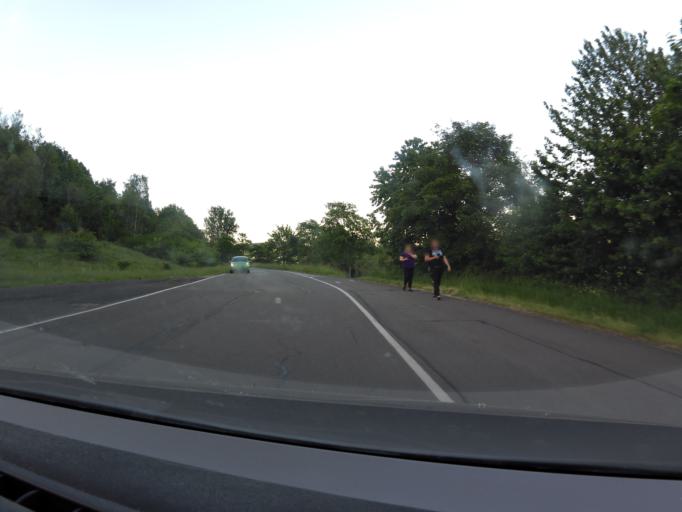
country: DE
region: Thuringia
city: Vacha
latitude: 50.8317
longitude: 10.0266
